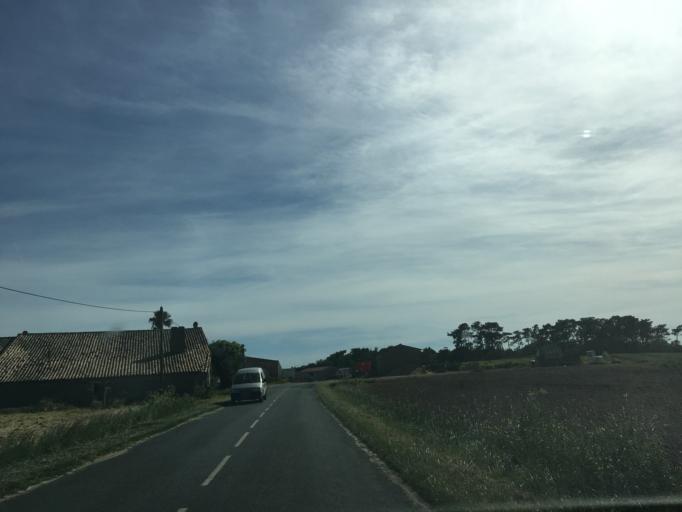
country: FR
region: Poitou-Charentes
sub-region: Departement de la Charente-Maritime
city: Mirambeau
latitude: 45.3363
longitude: -0.5918
